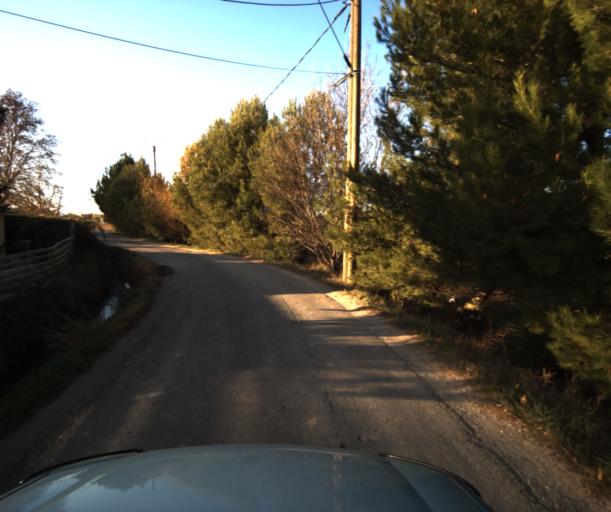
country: FR
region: Provence-Alpes-Cote d'Azur
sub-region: Departement du Vaucluse
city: Pertuis
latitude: 43.6726
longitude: 5.5290
